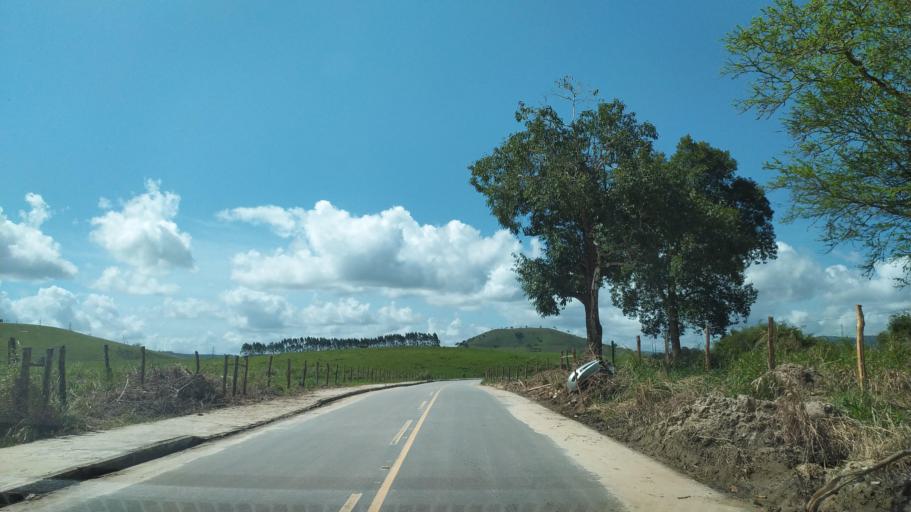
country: BR
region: Alagoas
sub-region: Uniao Dos Palmares
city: Uniao dos Palmares
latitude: -9.1585
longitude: -36.0442
